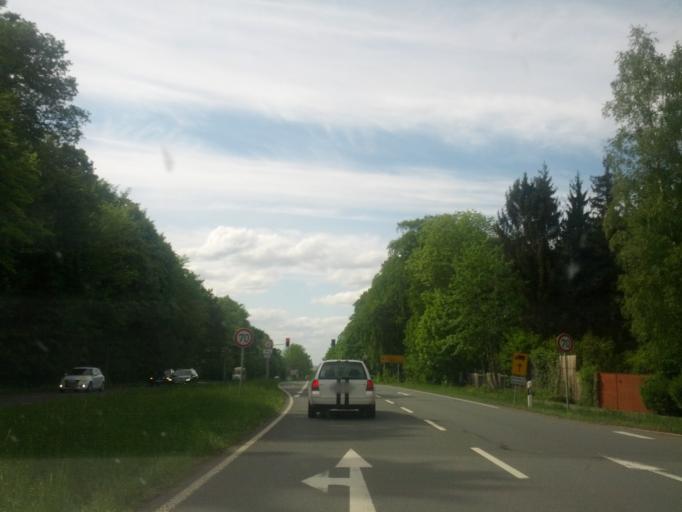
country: DE
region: Thuringia
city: Erfurt
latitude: 50.9424
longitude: 11.0359
